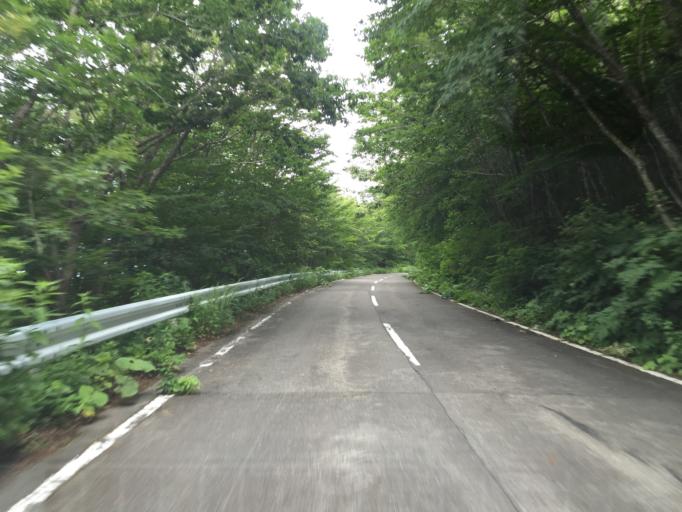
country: JP
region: Fukushima
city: Nihommatsu
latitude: 37.6567
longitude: 140.3031
